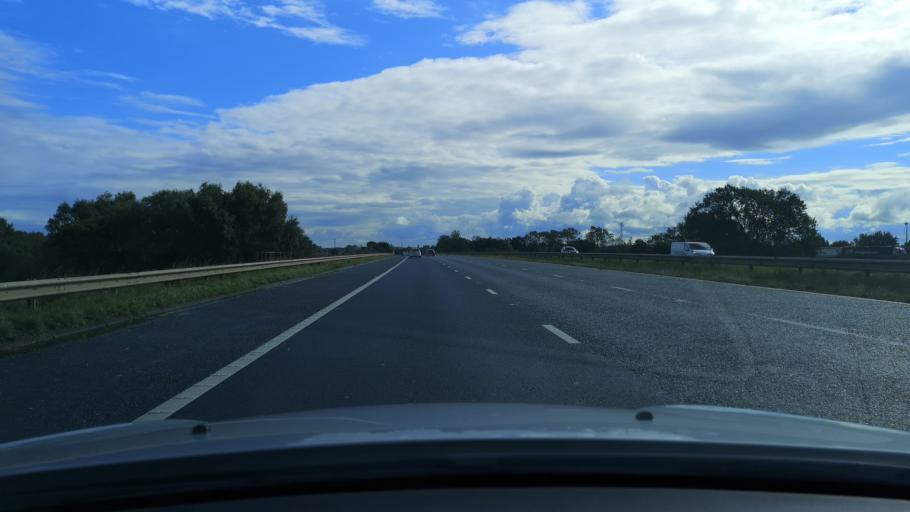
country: GB
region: England
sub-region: East Riding of Yorkshire
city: Pollington
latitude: 53.6887
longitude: -1.1009
